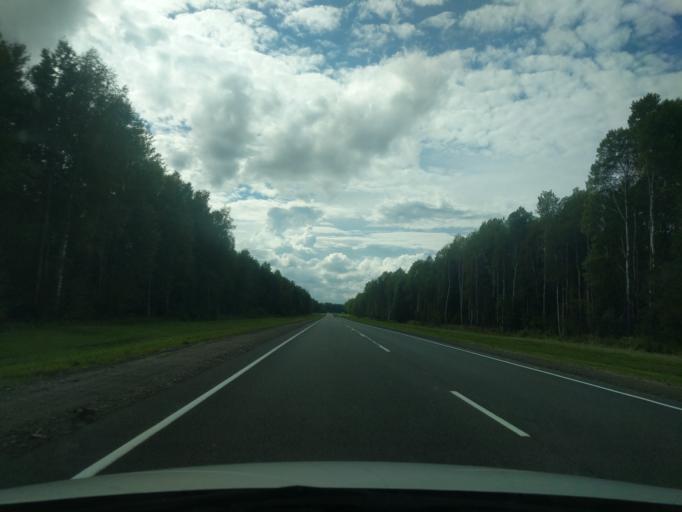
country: RU
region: Jaroslavl
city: Nekrasovskoye
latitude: 57.6369
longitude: 40.4390
